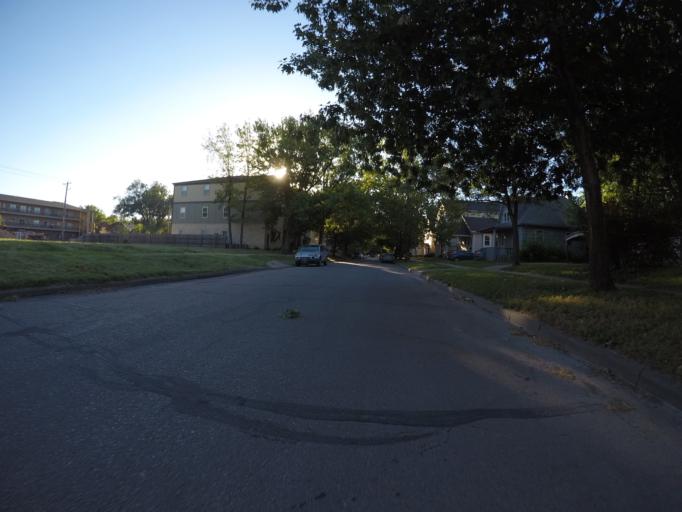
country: US
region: Kansas
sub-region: Riley County
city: Manhattan
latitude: 39.1889
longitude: -96.5714
